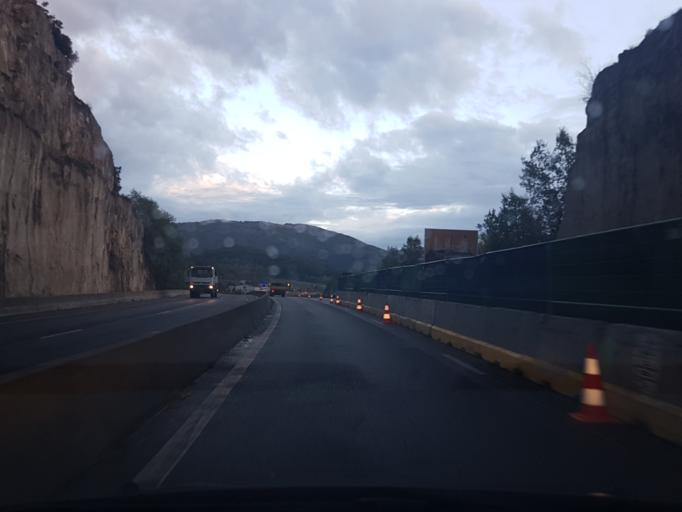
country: FR
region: Midi-Pyrenees
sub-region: Departement de l'Ariege
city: Varilhes
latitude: 43.0111
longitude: 1.6132
